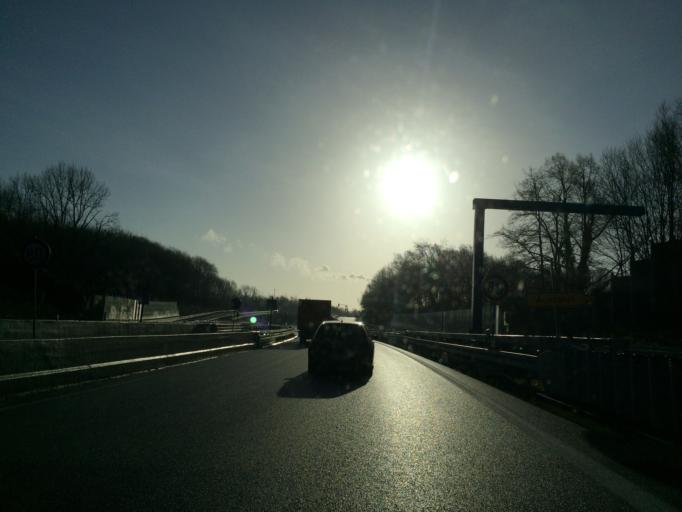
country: DE
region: North Rhine-Westphalia
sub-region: Regierungsbezirk Arnsberg
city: Bochum
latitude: 51.4573
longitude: 7.2064
